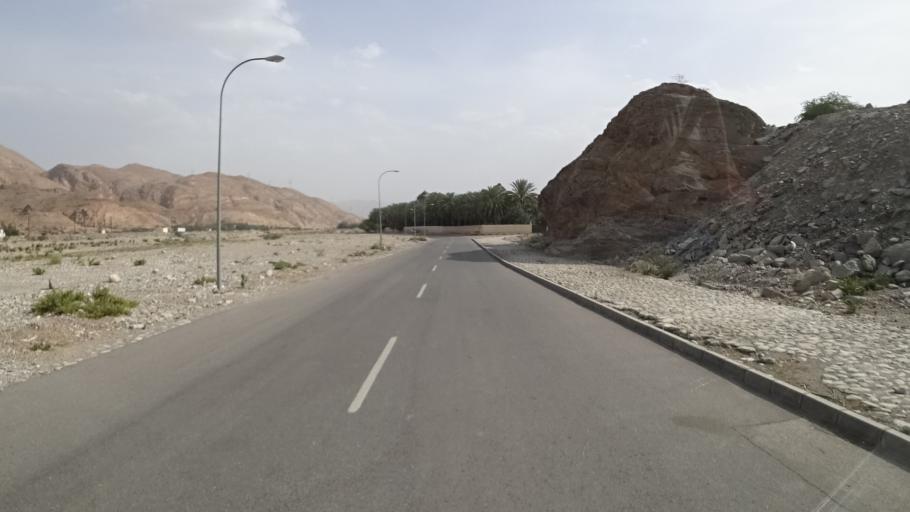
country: OM
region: Muhafazat Masqat
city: Bawshar
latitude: 23.3986
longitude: 58.5196
